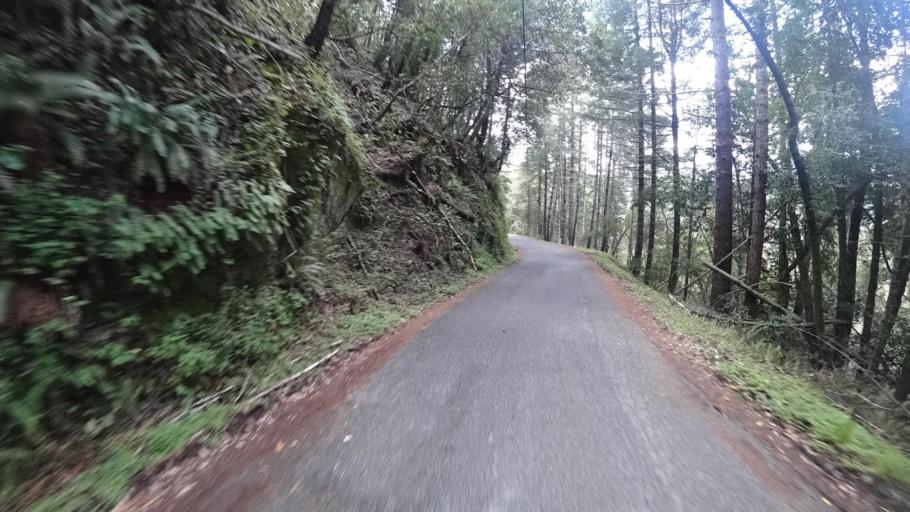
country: US
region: California
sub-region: Humboldt County
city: Blue Lake
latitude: 40.7647
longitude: -123.9275
